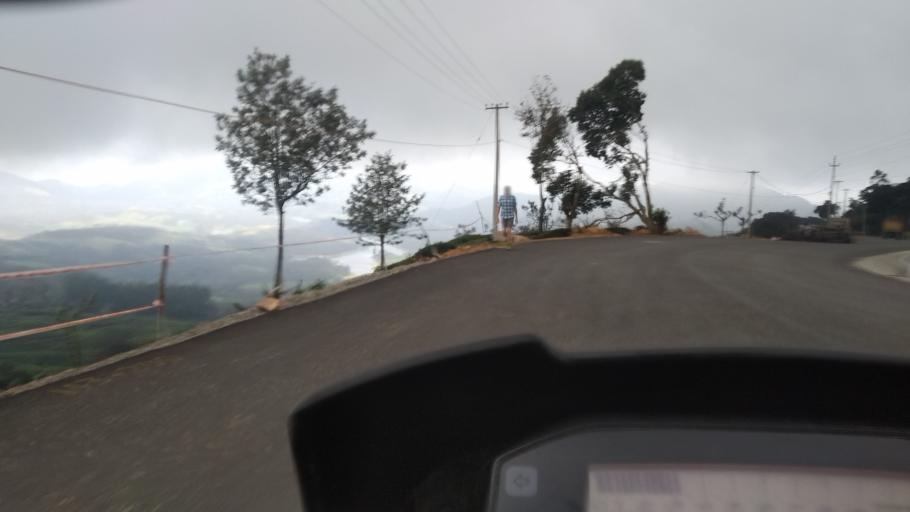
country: IN
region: Kerala
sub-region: Idukki
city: Munnar
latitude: 10.0342
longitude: 77.1598
